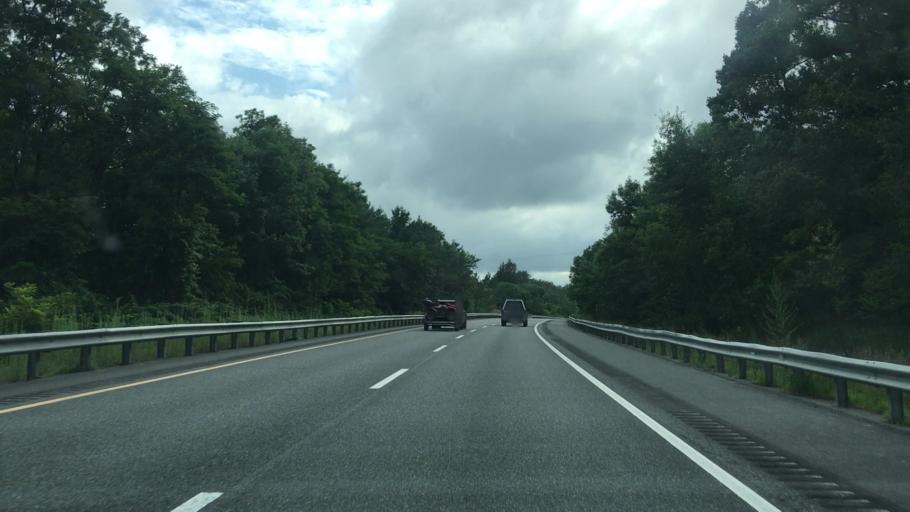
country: US
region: Maine
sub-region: Somerset County
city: Fairfield
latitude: 44.6036
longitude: -69.5809
